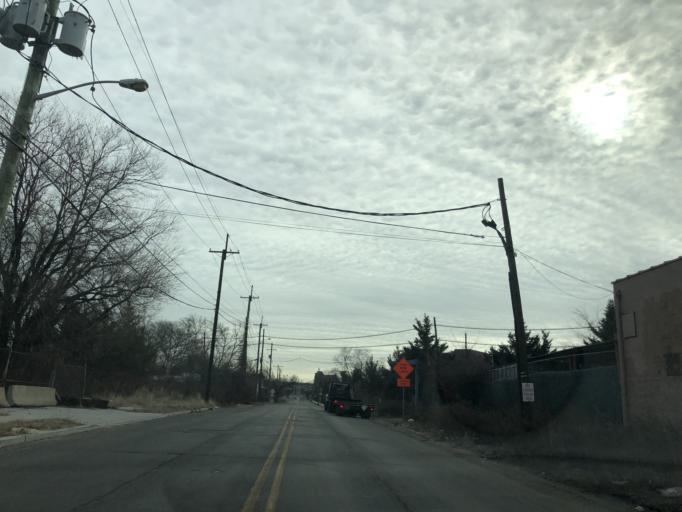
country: US
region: New Jersey
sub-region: Camden County
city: Camden
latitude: 39.9256
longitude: -75.1238
